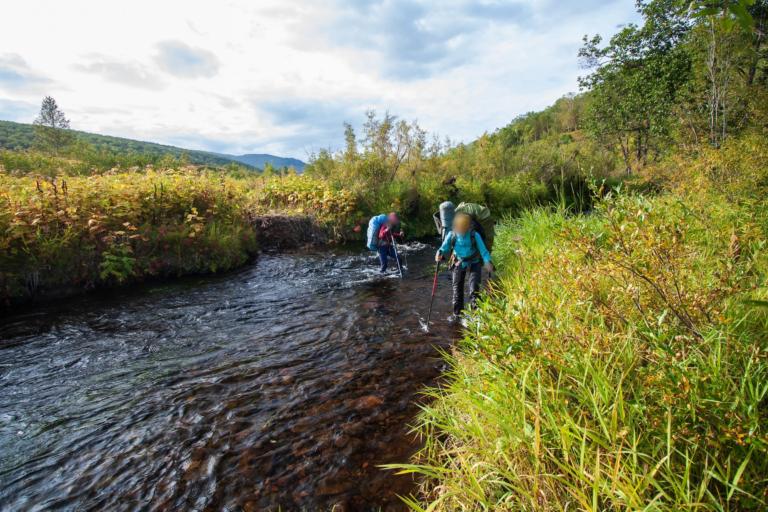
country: RU
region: Kamtsjatka
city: Yelizovo
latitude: 53.7635
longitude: 158.6117
